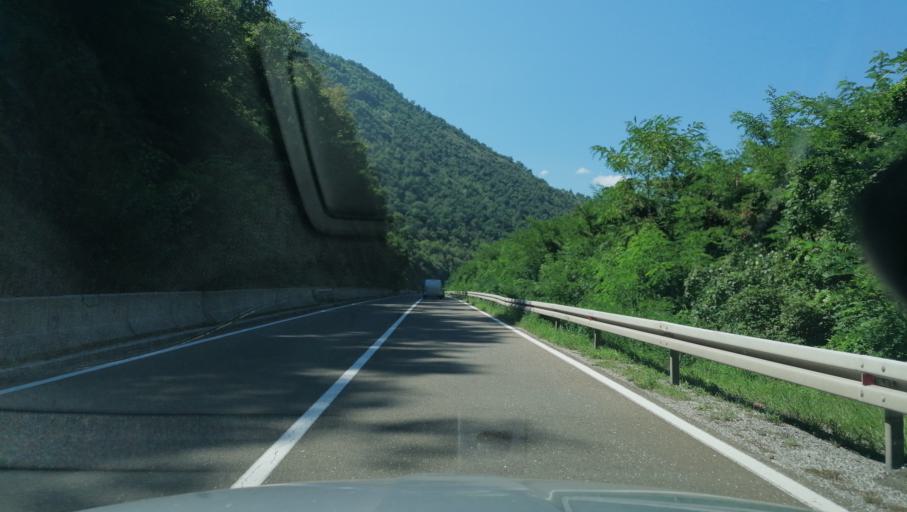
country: RS
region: Central Serbia
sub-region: Raski Okrug
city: Kraljevo
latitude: 43.5878
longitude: 20.5786
